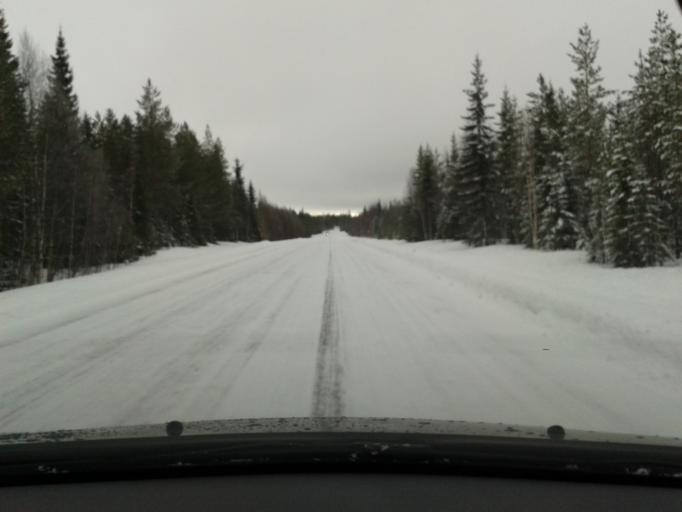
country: SE
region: Vaesterbotten
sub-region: Vilhelmina Kommun
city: Sjoberg
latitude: 64.8739
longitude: 15.8826
